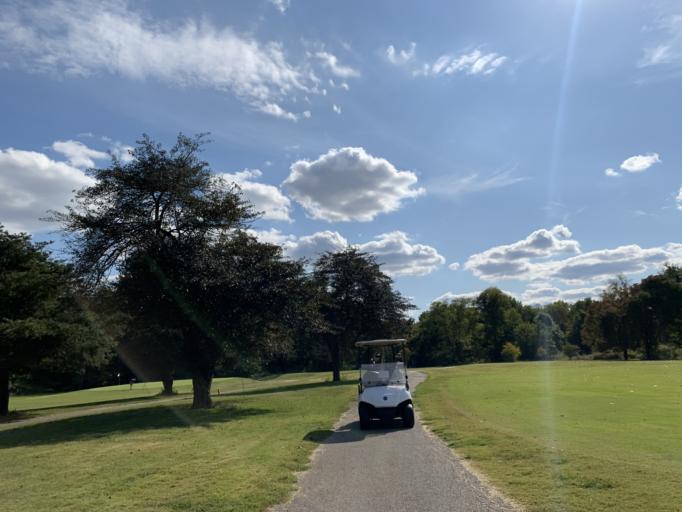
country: US
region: Indiana
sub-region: Floyd County
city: New Albany
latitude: 38.2671
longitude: -85.8284
